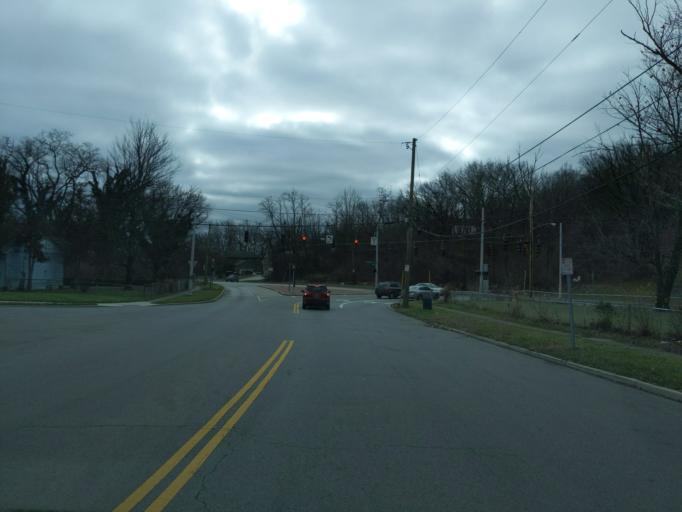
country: US
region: Ohio
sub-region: Hamilton County
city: Finneytown
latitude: 39.1747
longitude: -84.5475
